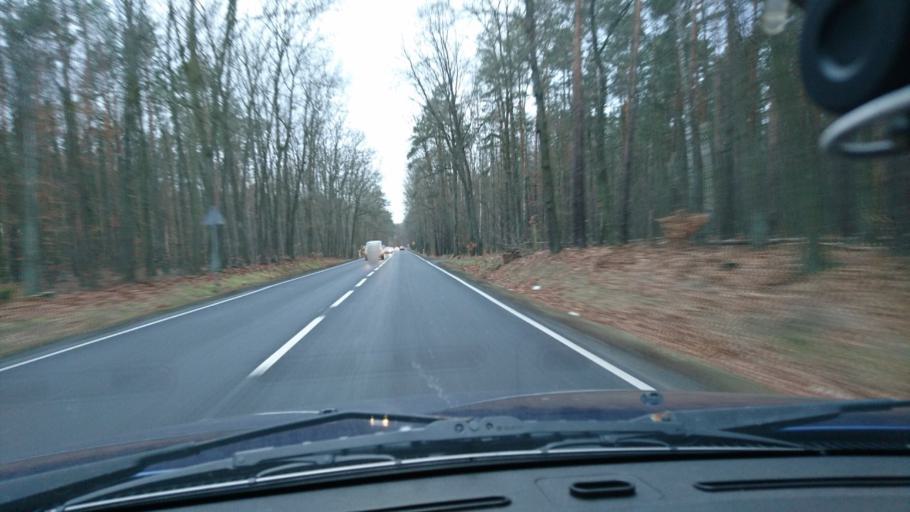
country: PL
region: Opole Voivodeship
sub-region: Powiat kluczborski
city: Kluczbork
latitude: 50.9611
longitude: 18.2972
